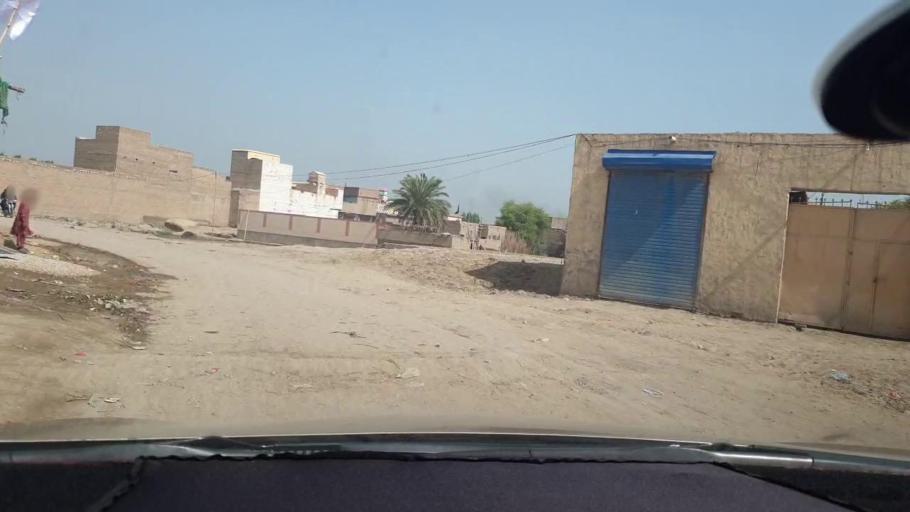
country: PK
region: Sindh
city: Kambar
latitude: 27.5811
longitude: 68.0062
